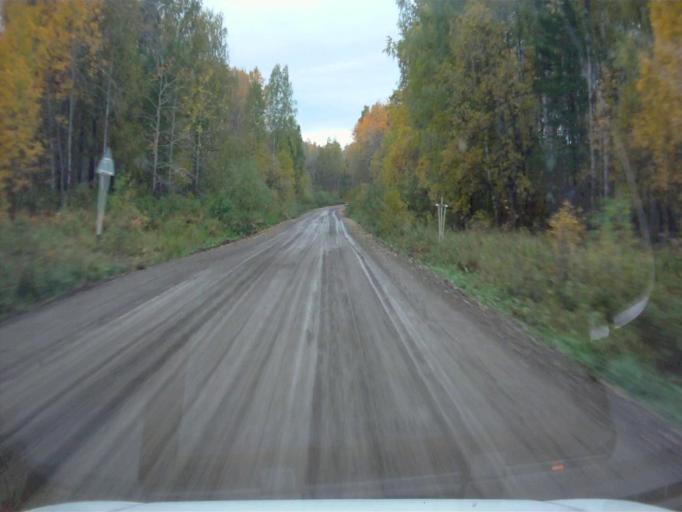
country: RU
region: Chelyabinsk
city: Nyazepetrovsk
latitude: 56.1132
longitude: 59.3693
